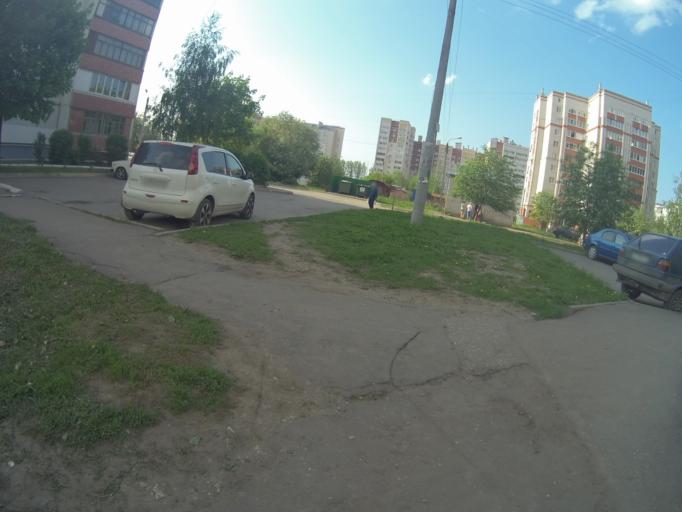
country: RU
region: Vladimir
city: Kommunar
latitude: 56.1707
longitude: 40.4518
